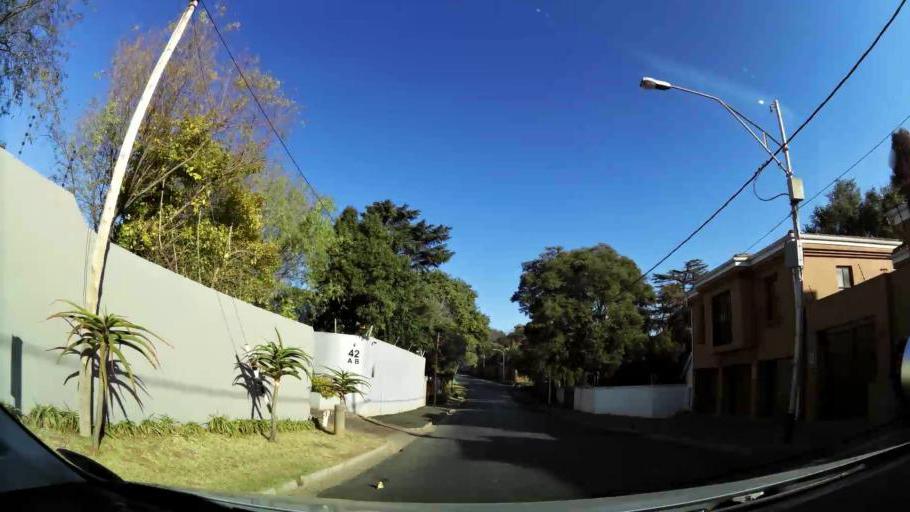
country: ZA
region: Gauteng
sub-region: City of Johannesburg Metropolitan Municipality
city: Johannesburg
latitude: -26.1500
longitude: 28.0731
